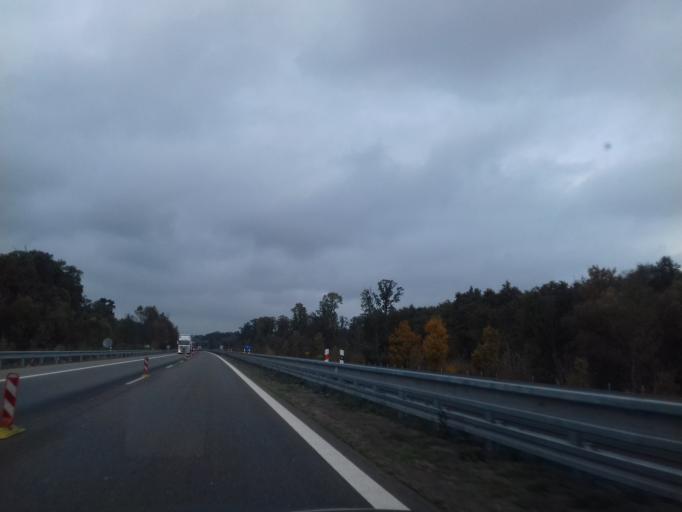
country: CZ
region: South Moravian
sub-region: Okres Breclav
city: Lanzhot
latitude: 48.7028
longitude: 16.9875
